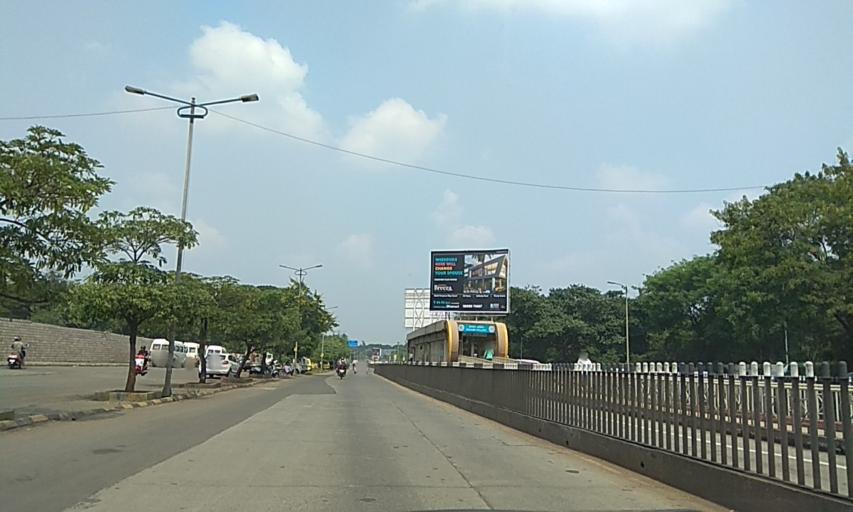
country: IN
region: Maharashtra
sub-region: Pune Division
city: Khadki
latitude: 18.5495
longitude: 73.8715
